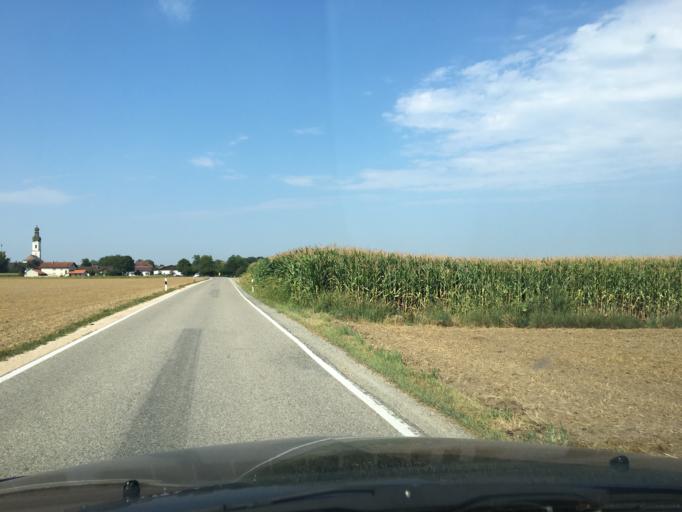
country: DE
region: Bavaria
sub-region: Upper Bavaria
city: Mettenheim
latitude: 48.2686
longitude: 12.4720
